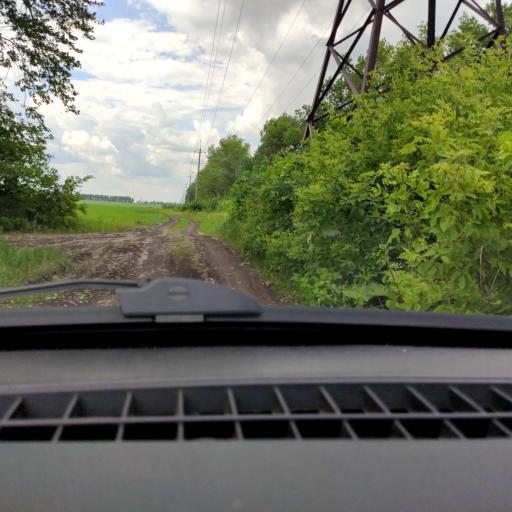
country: RU
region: Bashkortostan
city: Kabakovo
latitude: 54.5184
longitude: 56.0823
